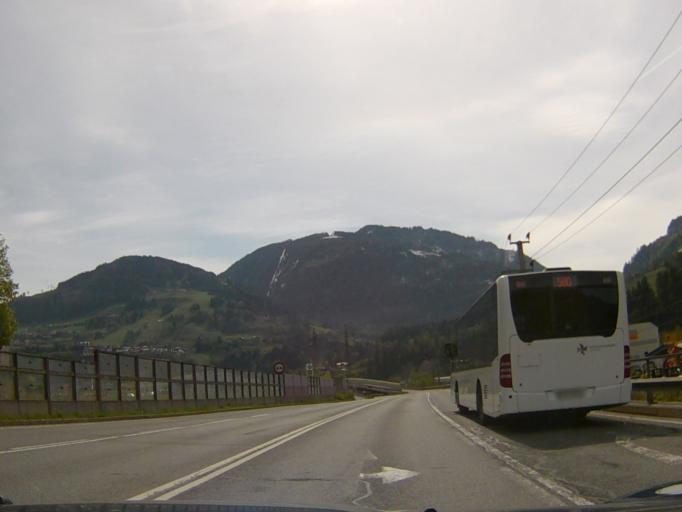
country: AT
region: Salzburg
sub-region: Politischer Bezirk Sankt Johann im Pongau
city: Schwarzach im Pongau
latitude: 47.3238
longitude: 13.1644
